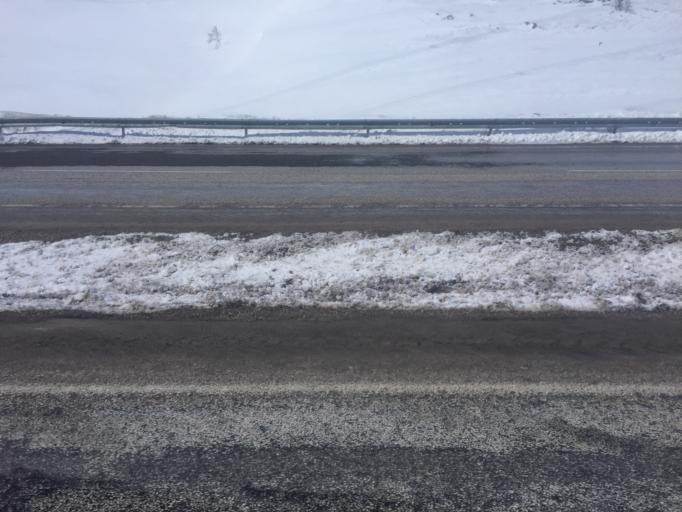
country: TR
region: Kahramanmaras
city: Goksun
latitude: 38.1931
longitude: 36.4569
